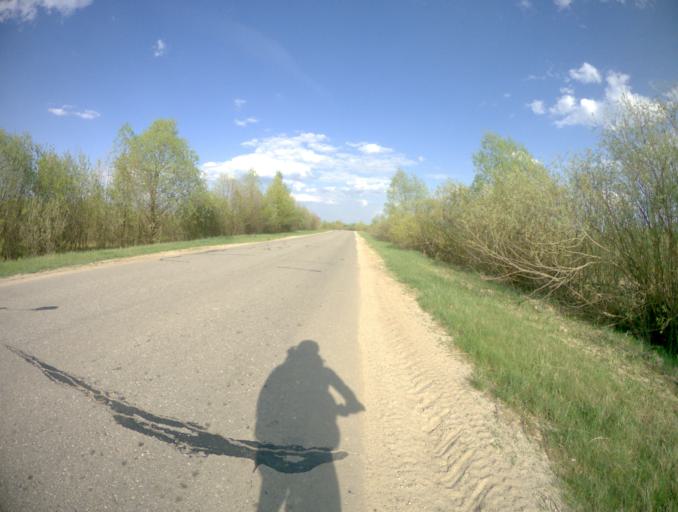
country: RU
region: Ivanovo
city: Kolobovo
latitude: 56.5405
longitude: 41.5274
